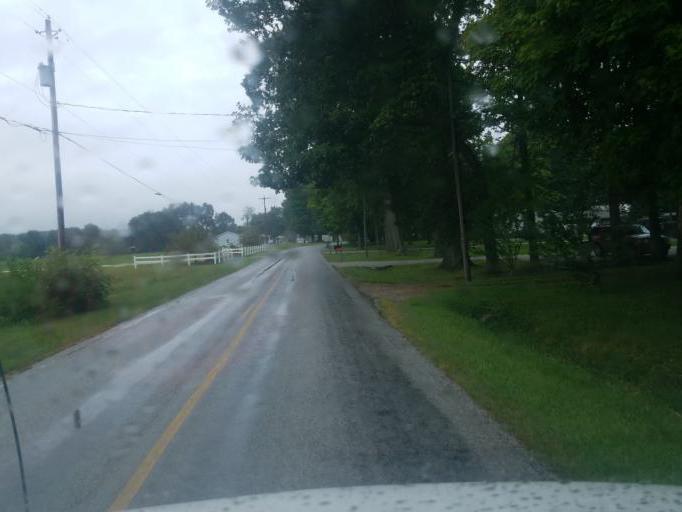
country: US
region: Ohio
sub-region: Wayne County
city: Creston
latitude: 40.9824
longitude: -81.8748
